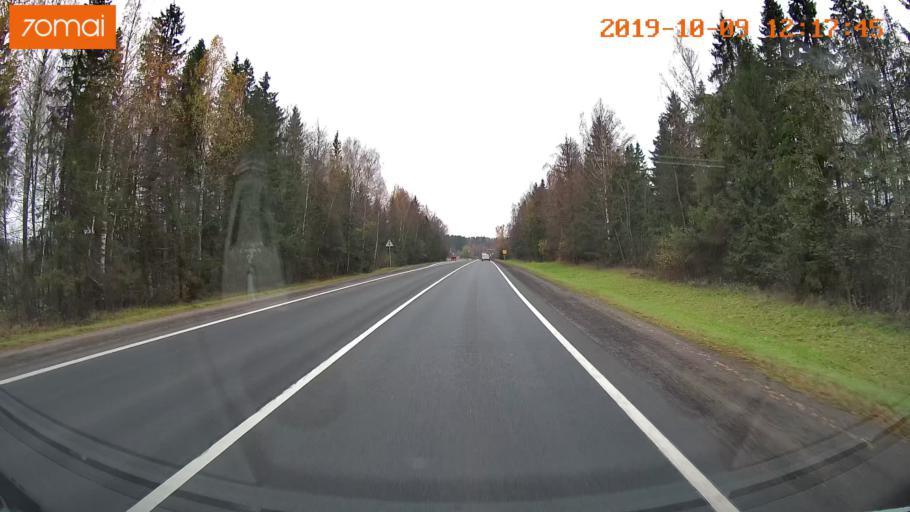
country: RU
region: Jaroslavl
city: Prechistoye
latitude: 58.4519
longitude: 40.3216
